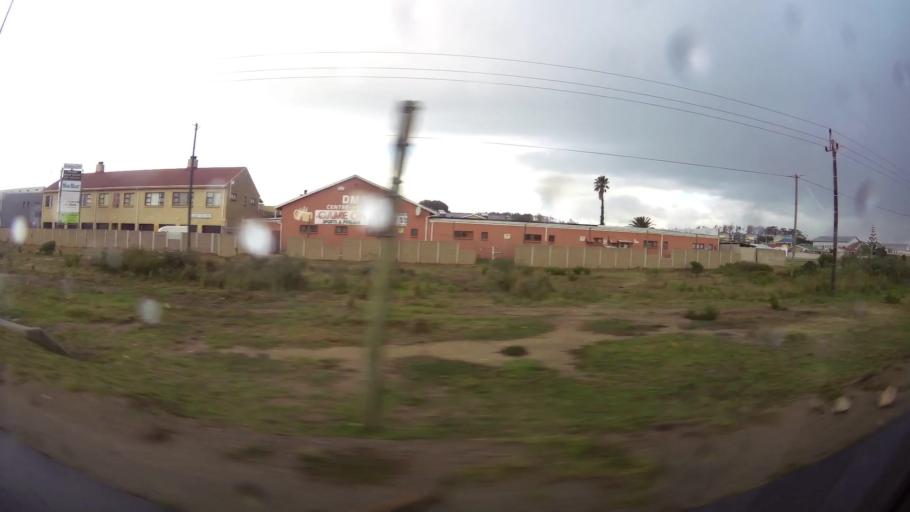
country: ZA
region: Western Cape
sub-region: Eden District Municipality
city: Mossel Bay
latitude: -34.1831
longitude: 22.1003
